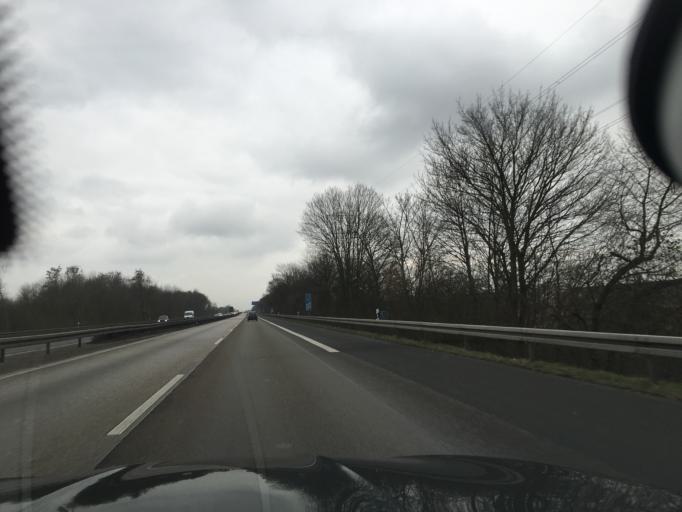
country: DE
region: North Rhine-Westphalia
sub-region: Regierungsbezirk Koln
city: Wahn-Heide
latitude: 50.8662
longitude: 7.0958
